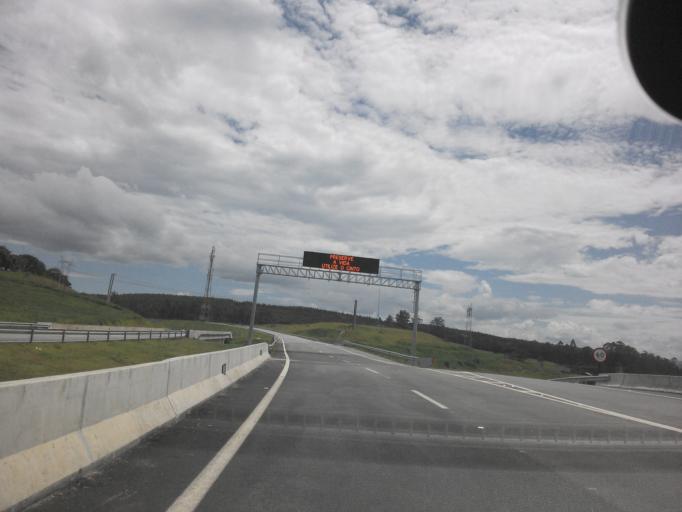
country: BR
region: Sao Paulo
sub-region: Taubate
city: Taubate
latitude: -23.0950
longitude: -45.6104
